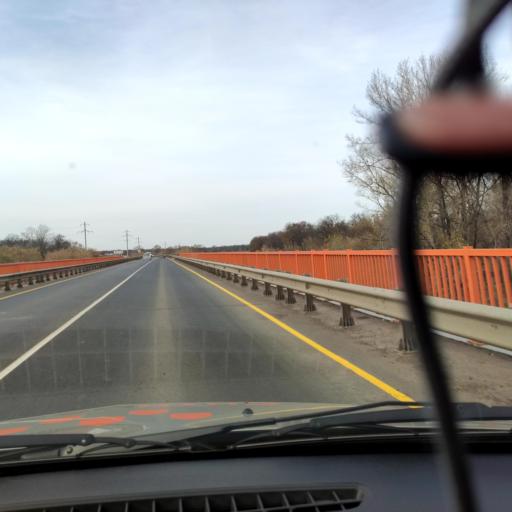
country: RU
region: Bashkortostan
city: Ufa
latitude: 54.5689
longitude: 55.9767
